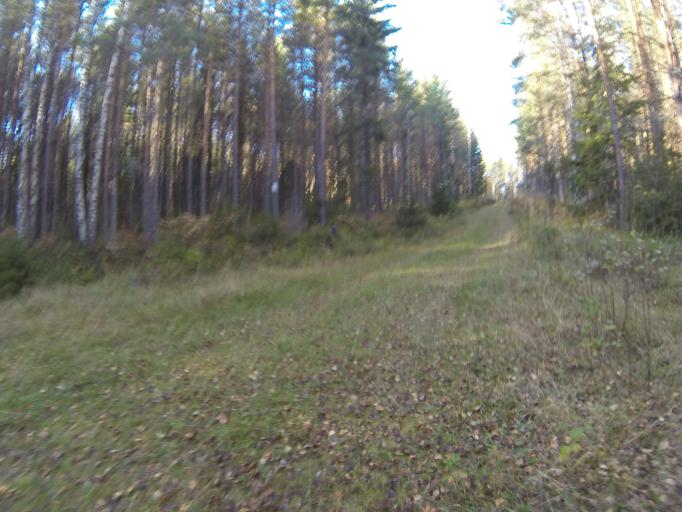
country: FI
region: Varsinais-Suomi
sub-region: Salo
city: Saerkisalo
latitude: 60.2238
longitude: 22.9602
